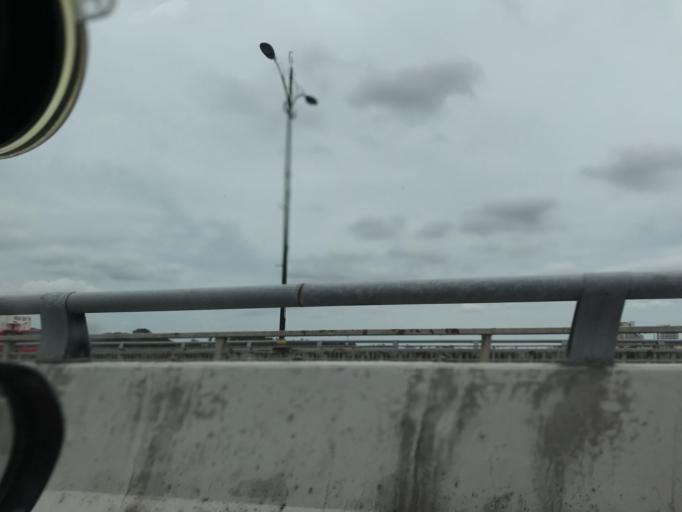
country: MY
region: Kelantan
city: Kota Bharu
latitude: 6.1162
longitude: 102.2292
